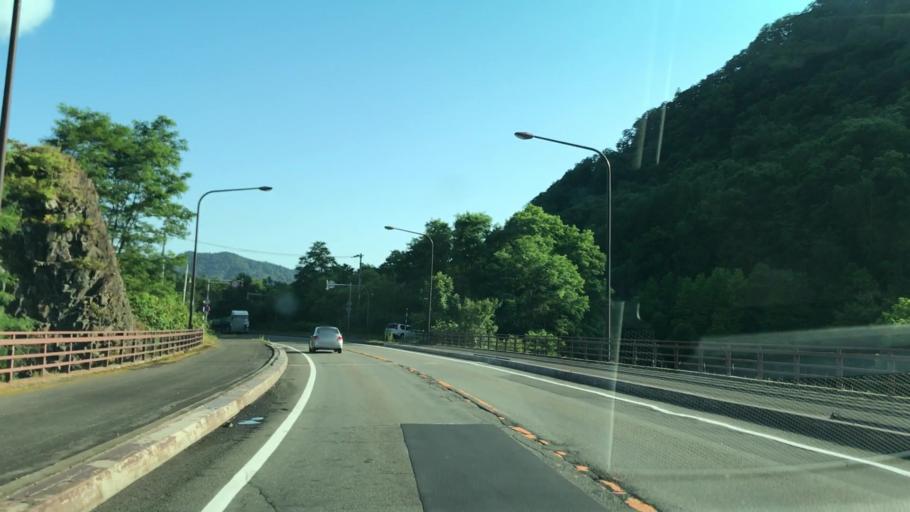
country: JP
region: Hokkaido
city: Iwamizawa
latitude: 42.9327
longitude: 142.0355
